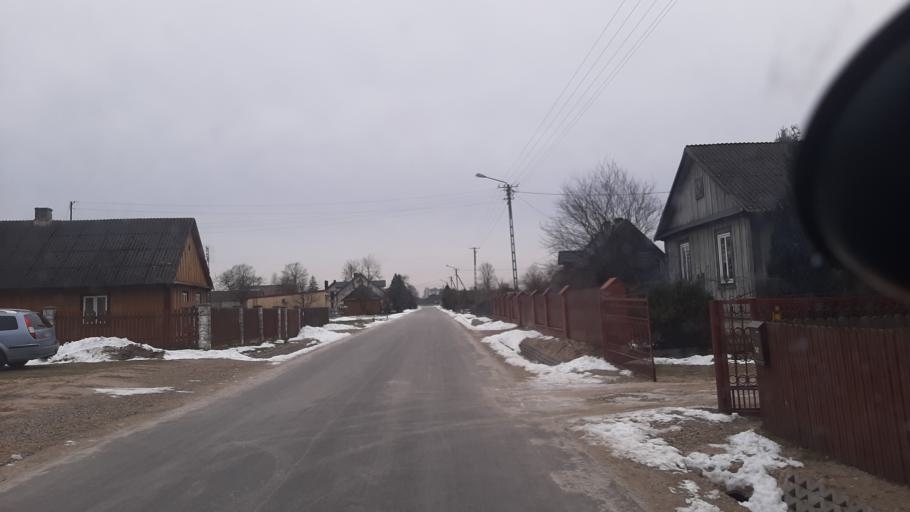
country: PL
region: Lublin Voivodeship
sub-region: Powiat lubartowski
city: Kamionka
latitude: 51.5158
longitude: 22.4732
